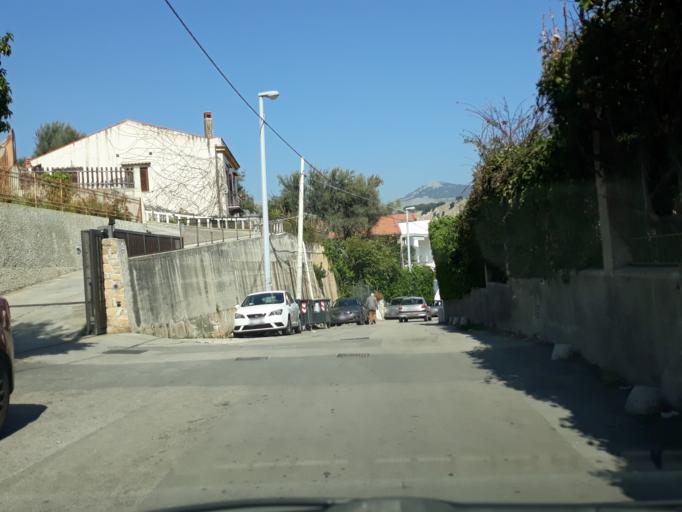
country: IT
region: Sicily
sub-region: Palermo
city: Piano dei Geli
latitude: 38.1110
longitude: 13.2987
